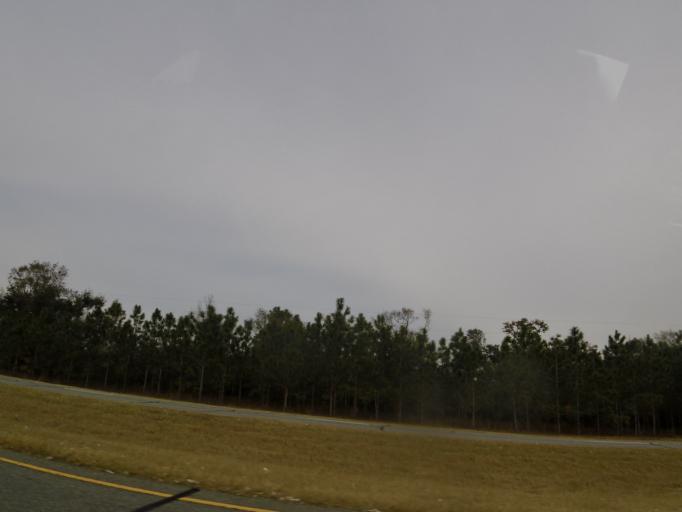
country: US
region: Georgia
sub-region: Seminole County
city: Donalsonville
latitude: 30.9909
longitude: -84.7620
